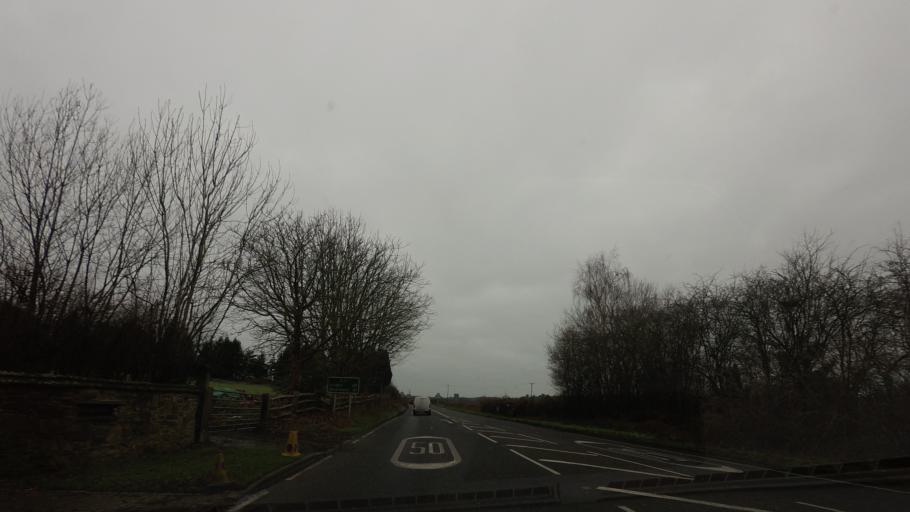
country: GB
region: England
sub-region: East Sussex
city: Battle
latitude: 50.9256
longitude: 0.5321
